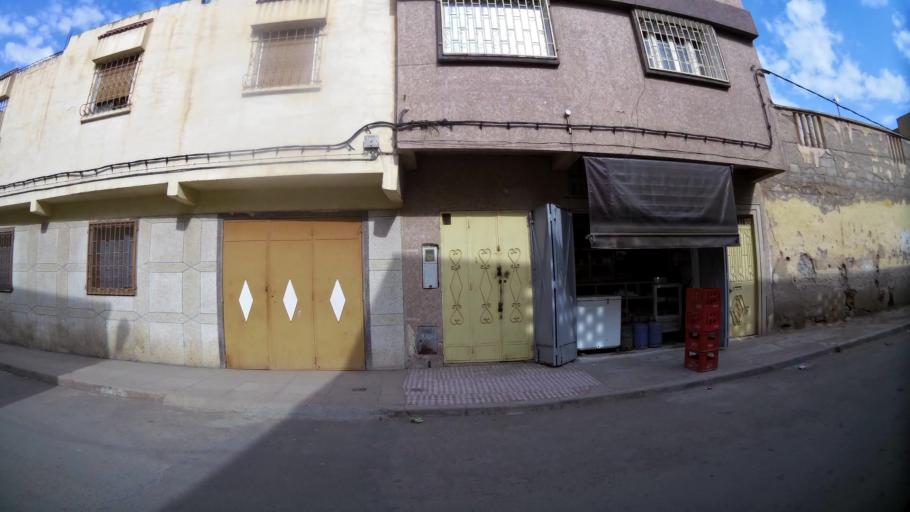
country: MA
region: Oriental
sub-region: Oujda-Angad
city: Oujda
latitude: 34.6897
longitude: -1.9043
